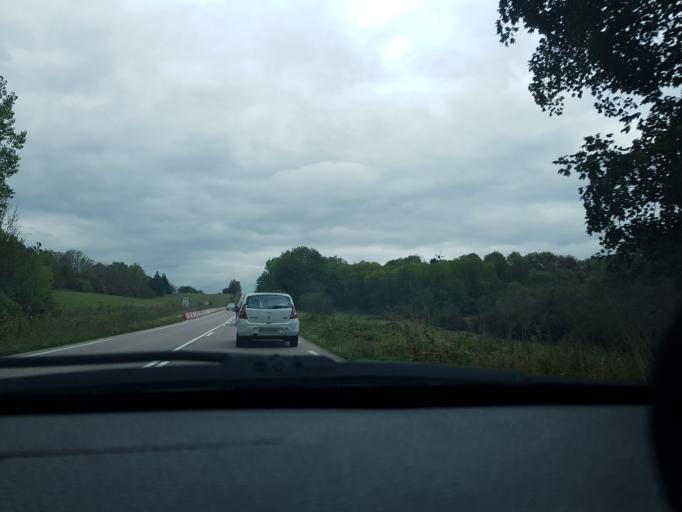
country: FR
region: Lorraine
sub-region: Departement de Meurthe-et-Moselle
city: Champenoux
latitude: 48.7669
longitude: 6.4374
